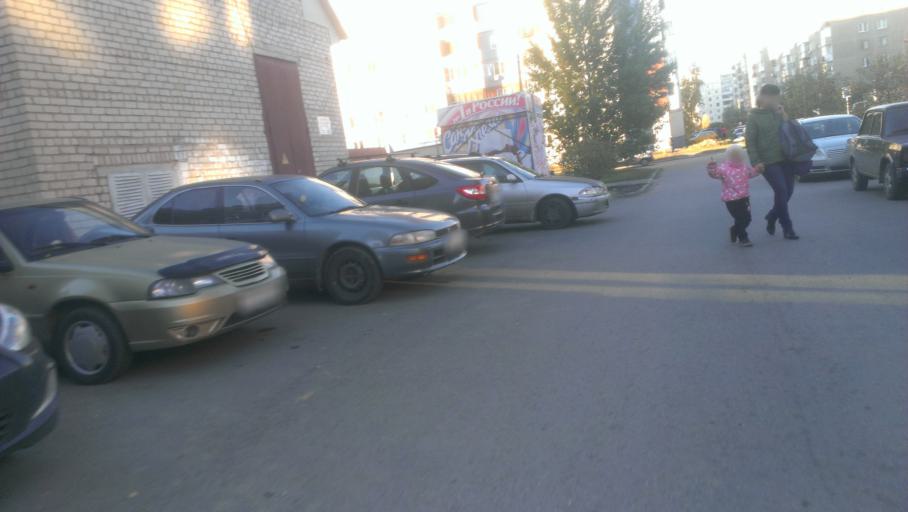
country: RU
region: Altai Krai
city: Novosilikatnyy
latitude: 53.3389
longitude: 83.6715
